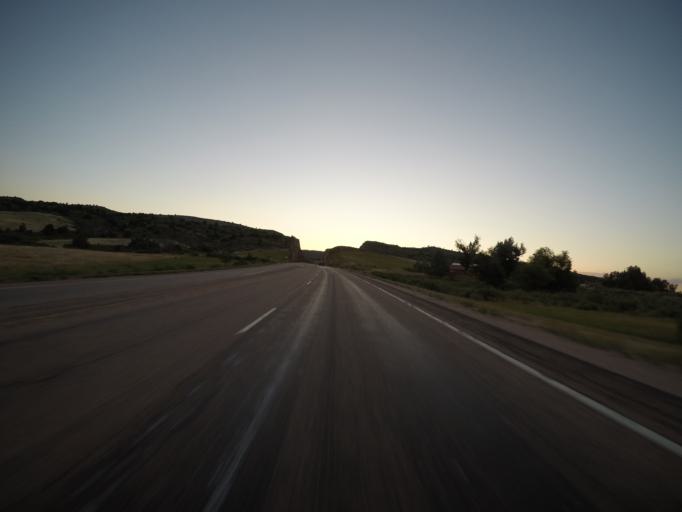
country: US
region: Colorado
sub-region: Larimer County
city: Laporte
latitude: 40.7610
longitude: -105.1755
